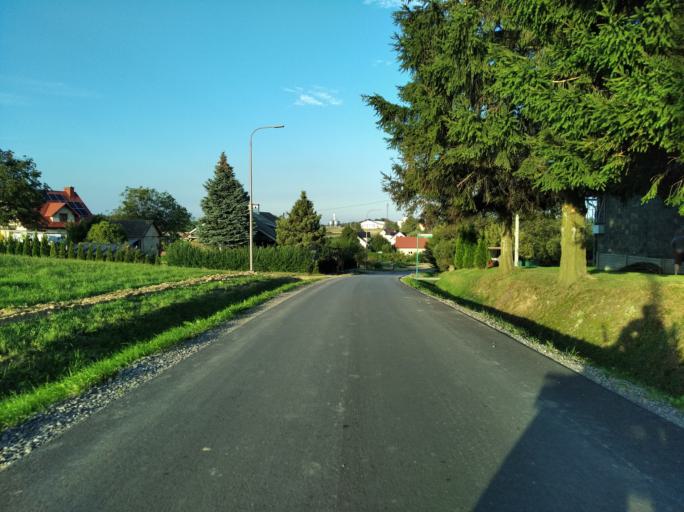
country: PL
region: Subcarpathian Voivodeship
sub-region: Powiat ropczycko-sedziszowski
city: Wielopole Skrzynskie
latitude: 49.9123
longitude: 21.6015
